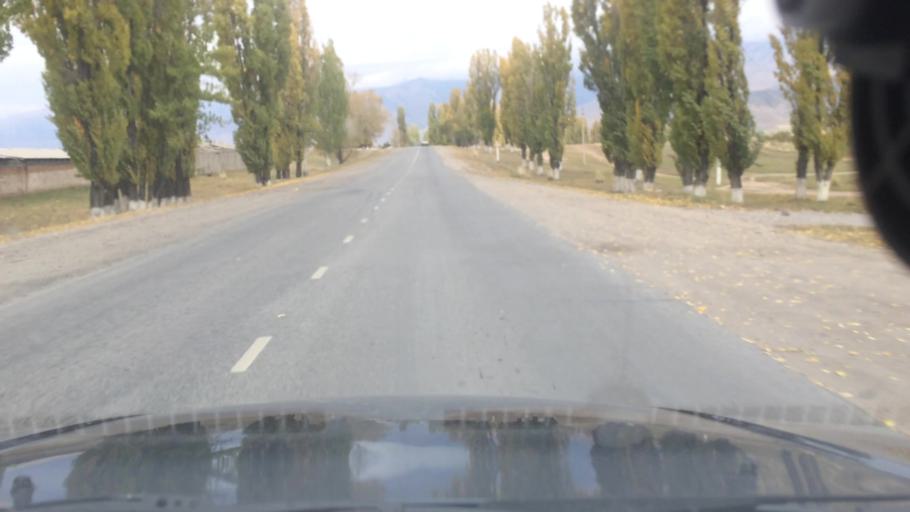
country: KG
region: Ysyk-Koel
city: Tyup
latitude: 42.7406
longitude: 78.3429
